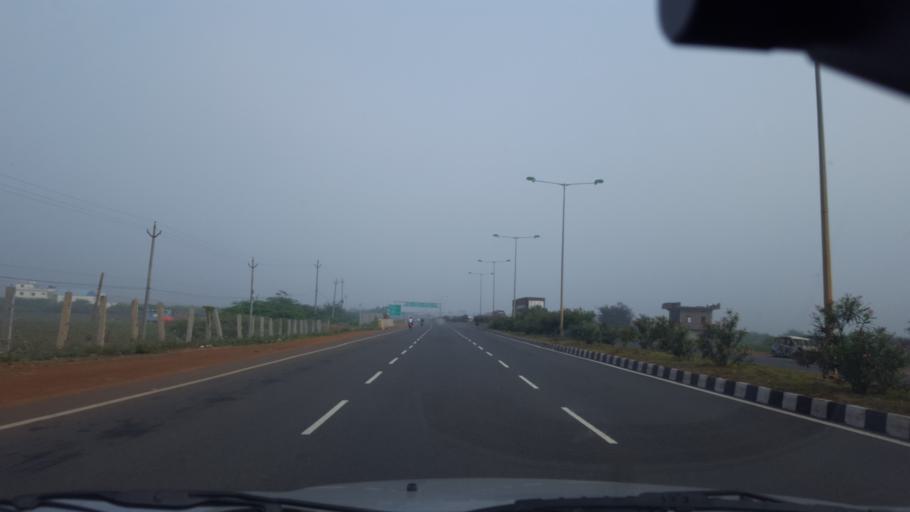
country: IN
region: Andhra Pradesh
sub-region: Prakasam
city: Ongole
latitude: 15.4631
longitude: 80.0483
